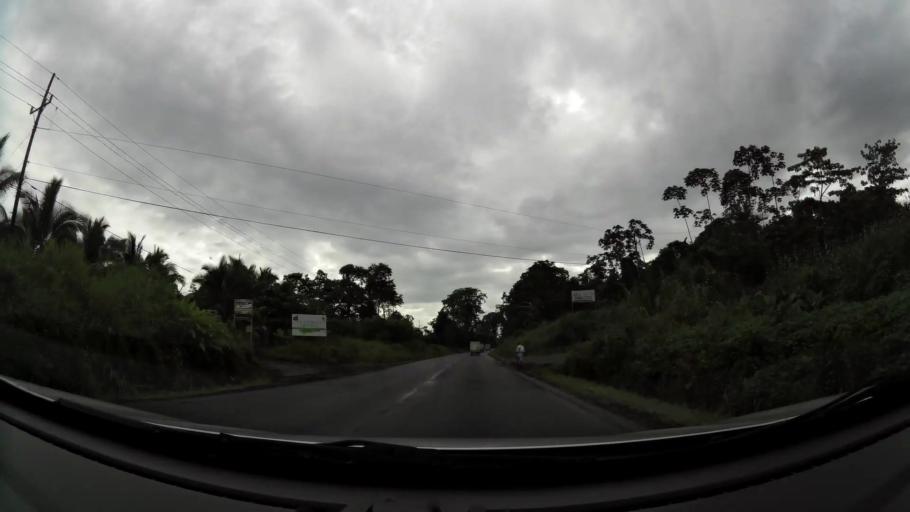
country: CR
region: Limon
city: Pocora
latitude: 10.1421
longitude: -83.5705
